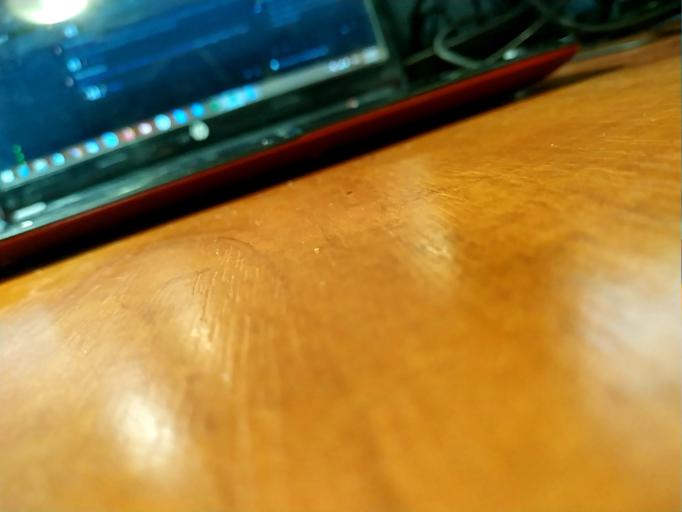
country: RU
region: Tverskaya
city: Sandovo
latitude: 58.6297
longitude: 36.4358
